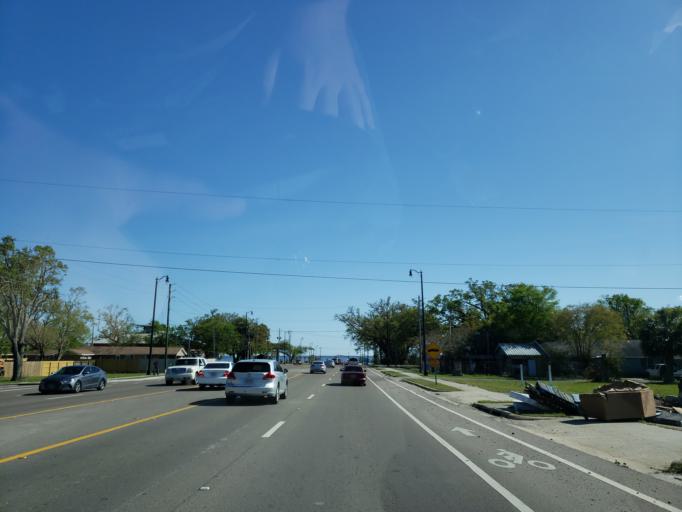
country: US
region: Mississippi
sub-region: Harrison County
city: Gulfport
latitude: 30.3864
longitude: -89.0270
